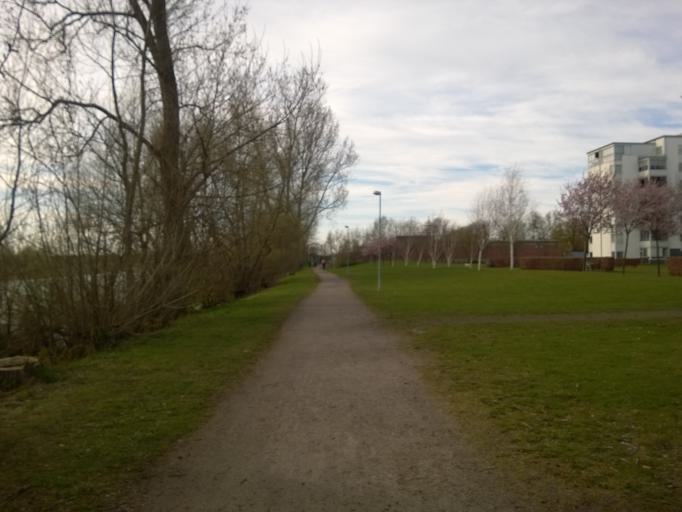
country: SE
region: Skane
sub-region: Kristianstads Kommun
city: Kristianstad
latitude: 56.0307
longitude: 14.1492
